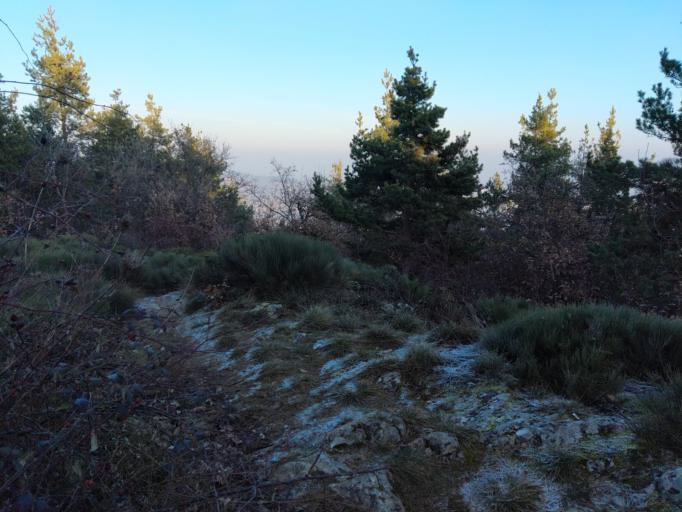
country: FR
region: Rhone-Alpes
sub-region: Departement de l'Ardeche
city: Boulieu-les-Annonay
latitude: 45.2551
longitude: 4.6494
